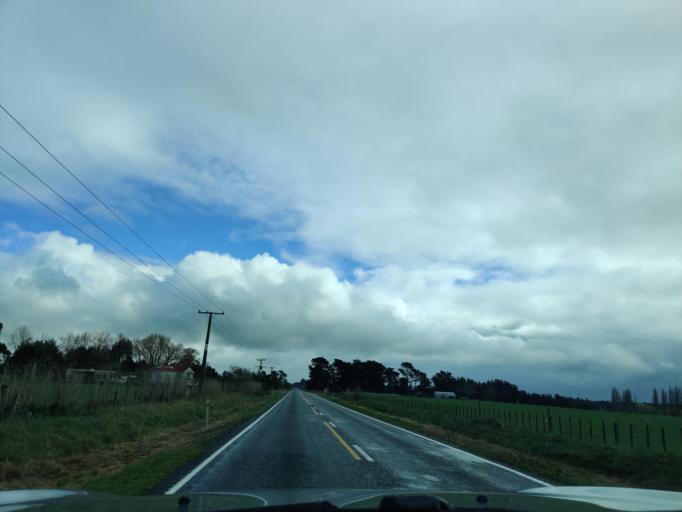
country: NZ
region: Hawke's Bay
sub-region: Hastings District
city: Hastings
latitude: -40.0170
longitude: 176.3529
